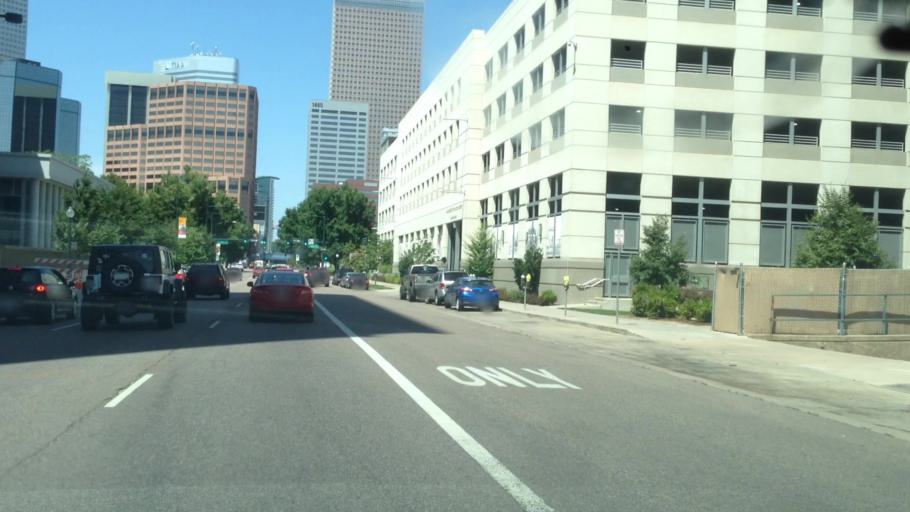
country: US
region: Colorado
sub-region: Denver County
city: Denver
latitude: 39.7370
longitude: -104.9861
